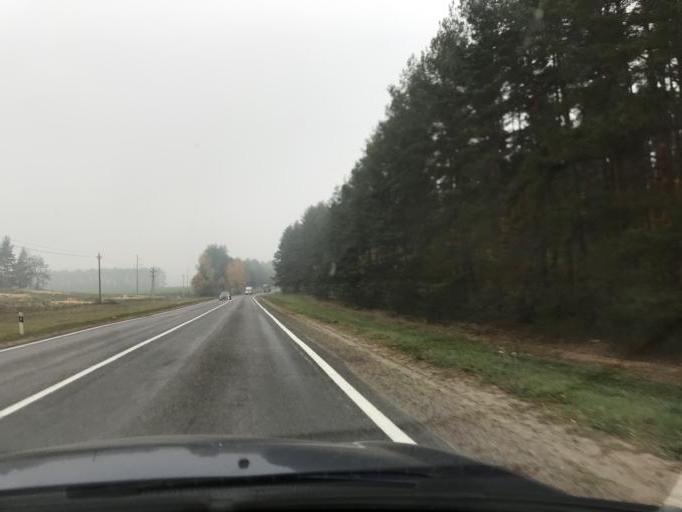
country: BY
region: Grodnenskaya
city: Hrodna
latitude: 53.7852
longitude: 23.8512
